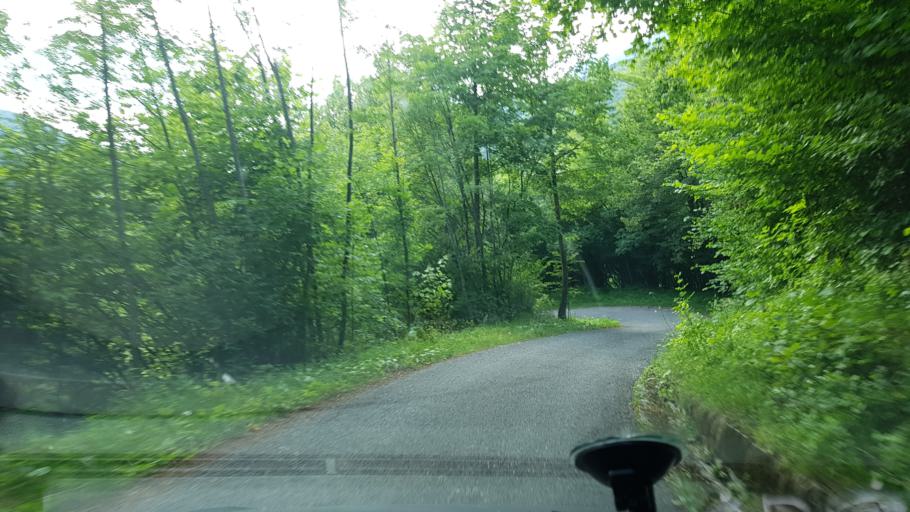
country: IT
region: Friuli Venezia Giulia
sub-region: Provincia di Udine
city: Prato
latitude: 46.3465
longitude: 13.3967
